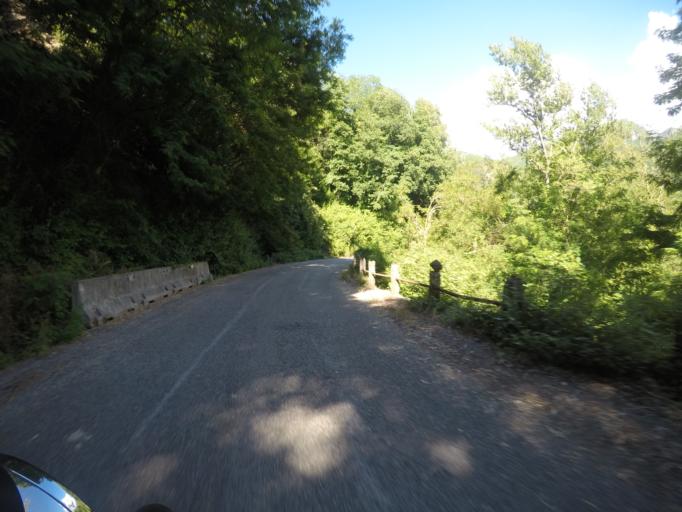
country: IT
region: Tuscany
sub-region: Provincia di Massa-Carrara
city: Fosdinovo
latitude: 44.1444
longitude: 10.0919
